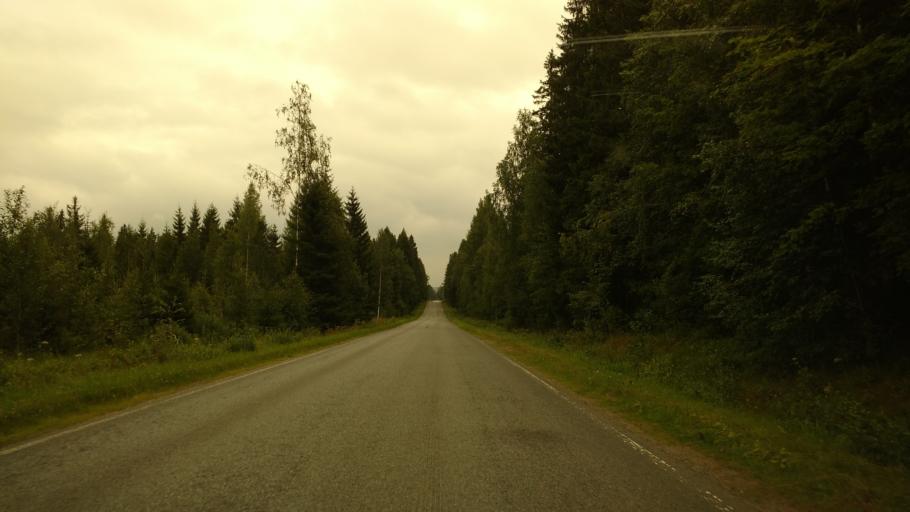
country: FI
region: Haeme
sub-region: Forssa
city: Ypaejae
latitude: 60.7754
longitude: 23.2549
